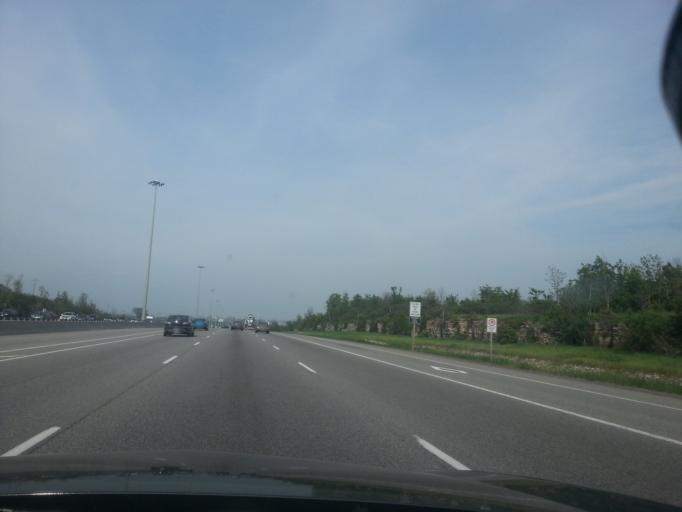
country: CA
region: Ontario
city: Bells Corners
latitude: 45.3276
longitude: -75.8677
